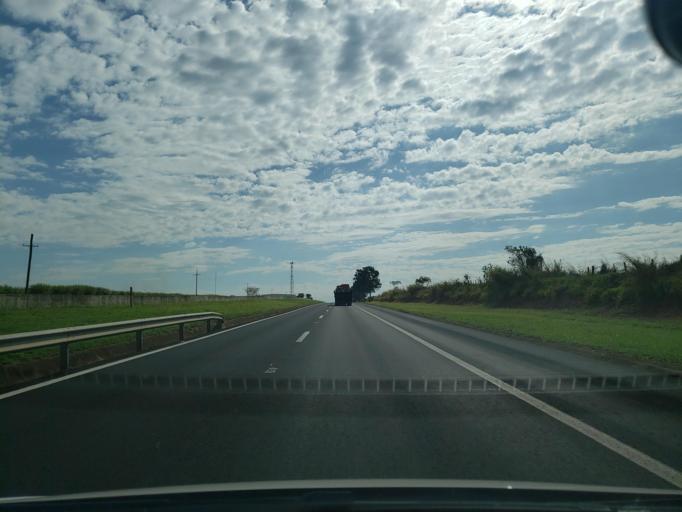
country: BR
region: Sao Paulo
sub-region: Lins
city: Lins
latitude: -21.6396
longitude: -49.8273
